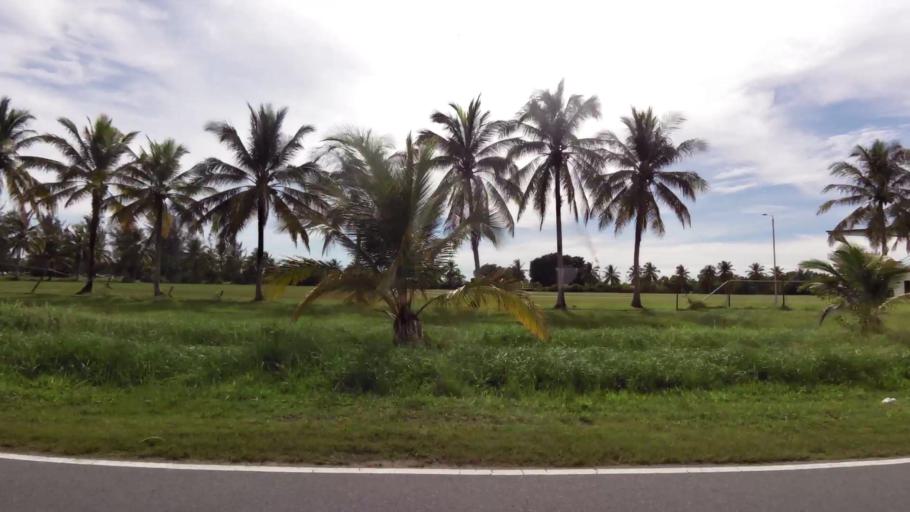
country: BN
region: Belait
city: Seria
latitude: 4.6174
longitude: 114.3292
